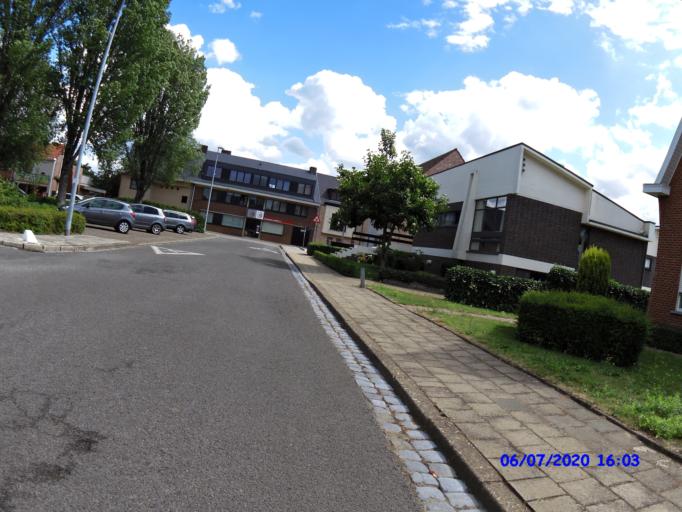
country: BE
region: Flanders
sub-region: Provincie Antwerpen
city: Balen
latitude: 51.1422
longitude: 5.1481
